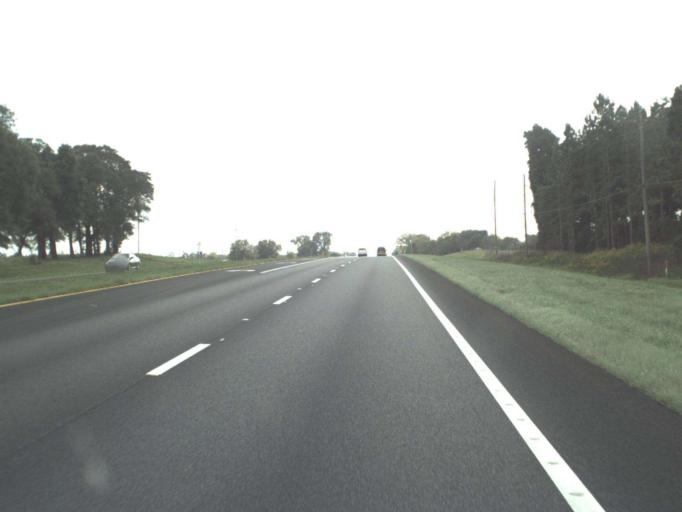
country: US
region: Florida
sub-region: Jackson County
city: Graceville
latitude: 30.9032
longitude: -85.3750
